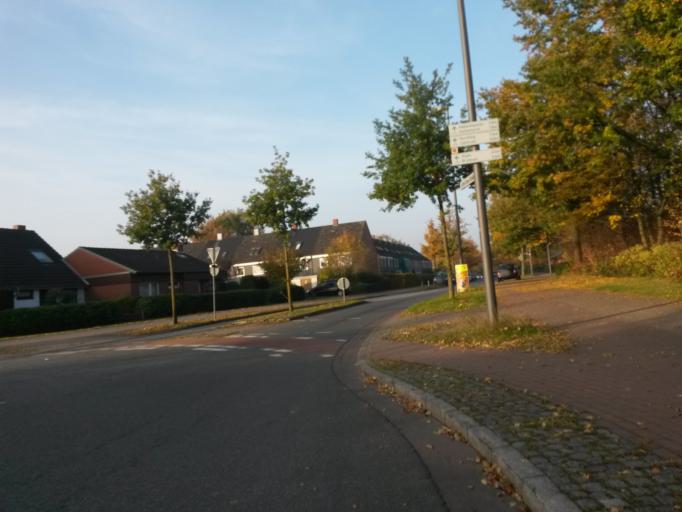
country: DE
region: Bremen
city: Bremen
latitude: 53.0271
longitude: 8.8231
